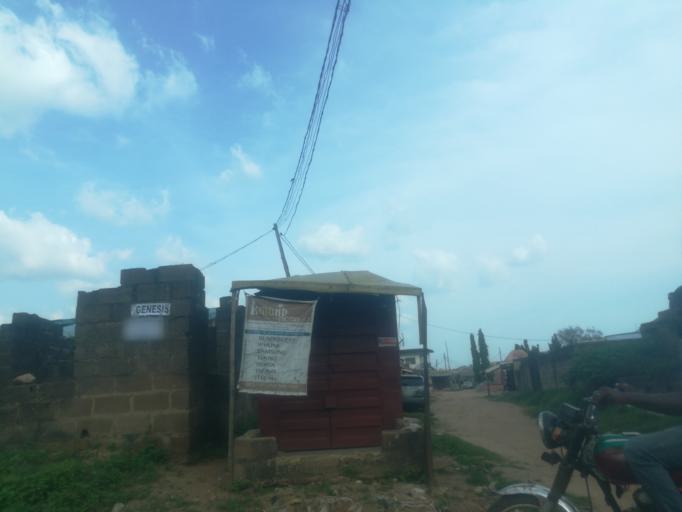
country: NG
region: Ogun
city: Abeokuta
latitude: 7.1163
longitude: 3.3268
